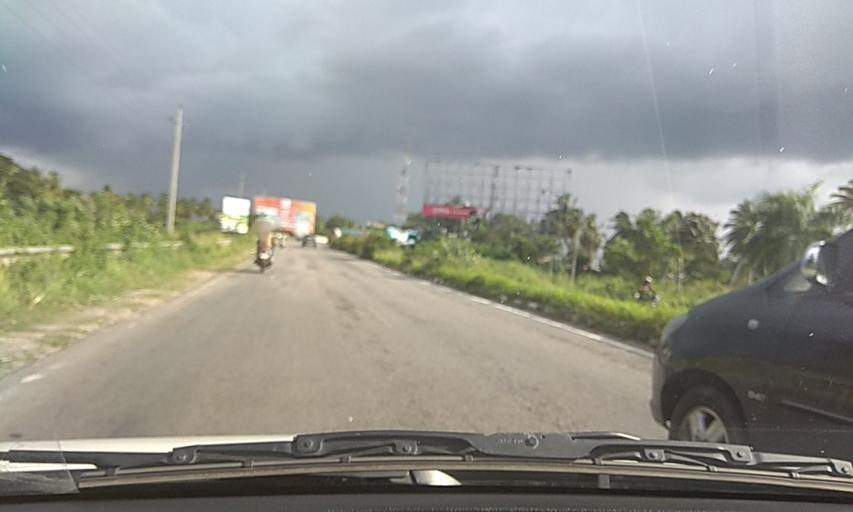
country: IN
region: Karnataka
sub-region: Mandya
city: Shrirangapattana
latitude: 12.4038
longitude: 76.6689
